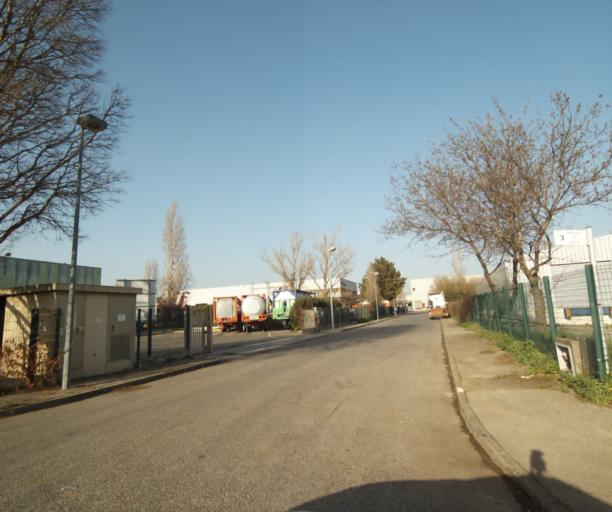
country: FR
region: Provence-Alpes-Cote d'Azur
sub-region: Departement des Bouches-du-Rhone
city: Saint-Victoret
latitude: 43.4171
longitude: 5.2696
